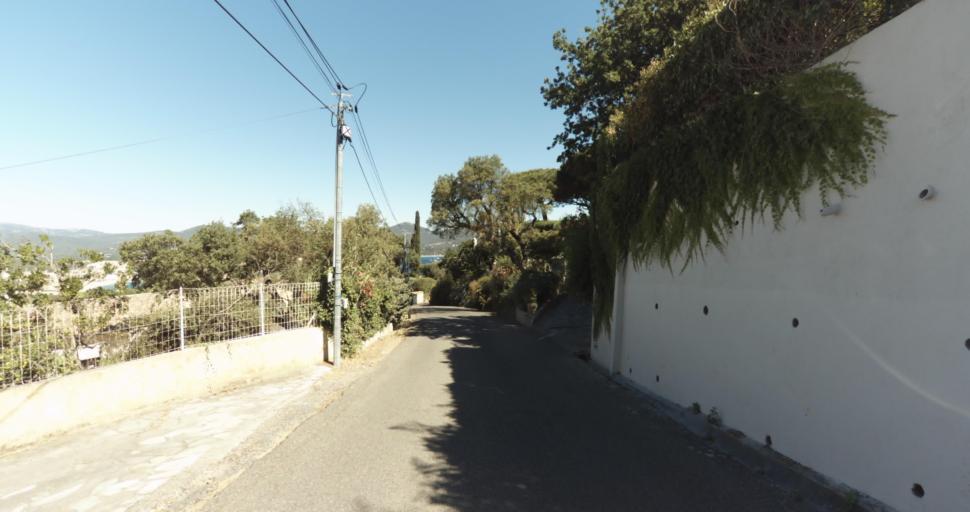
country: FR
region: Provence-Alpes-Cote d'Azur
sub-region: Departement du Var
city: Gassin
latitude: 43.2590
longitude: 6.6021
